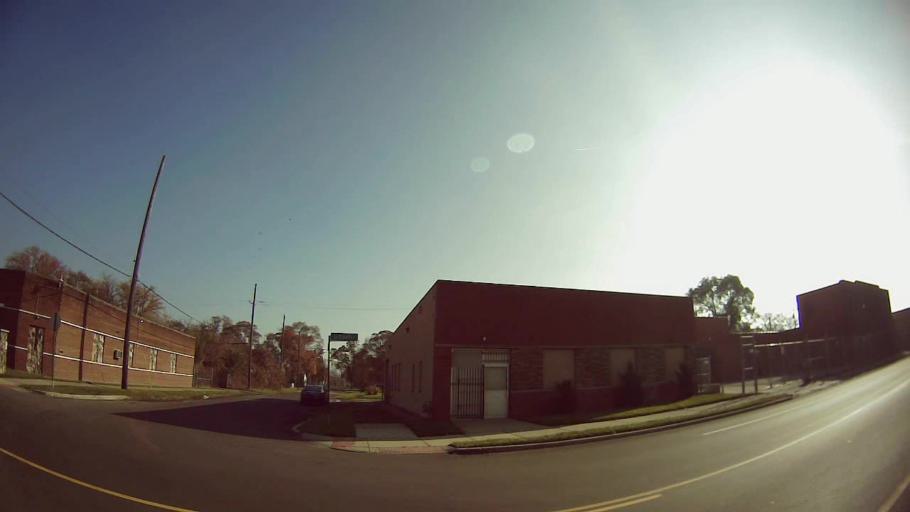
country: US
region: Michigan
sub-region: Oakland County
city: Oak Park
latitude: 42.3972
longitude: -83.1789
